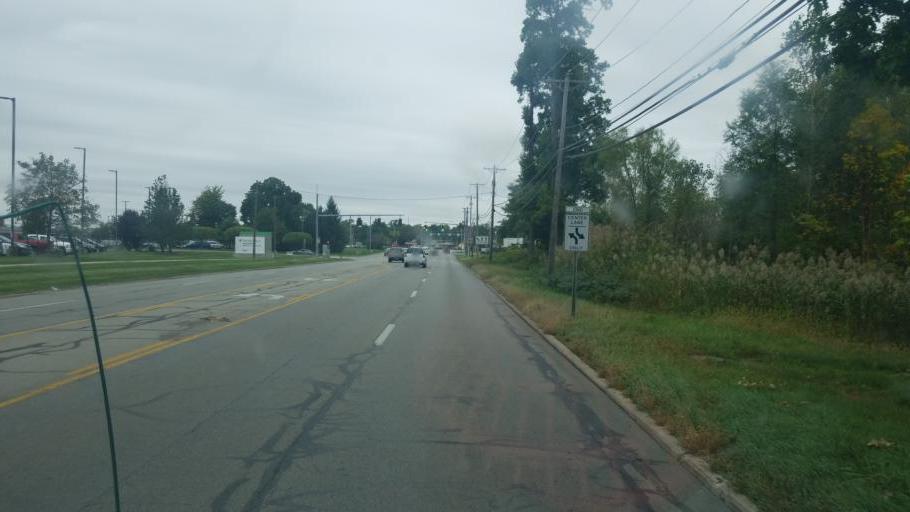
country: US
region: Ohio
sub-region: Lucas County
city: Ottawa Hills
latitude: 41.6739
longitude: -83.6702
